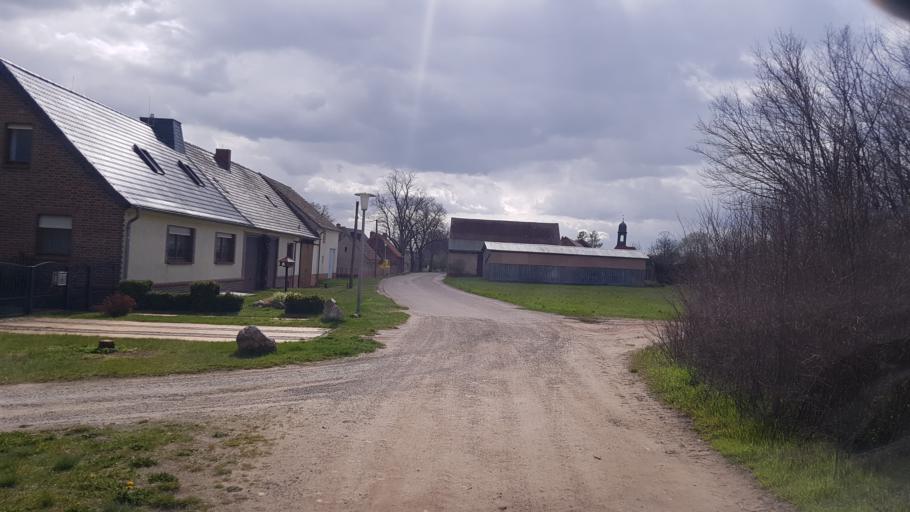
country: DE
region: Brandenburg
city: Calau
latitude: 51.7564
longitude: 14.0102
